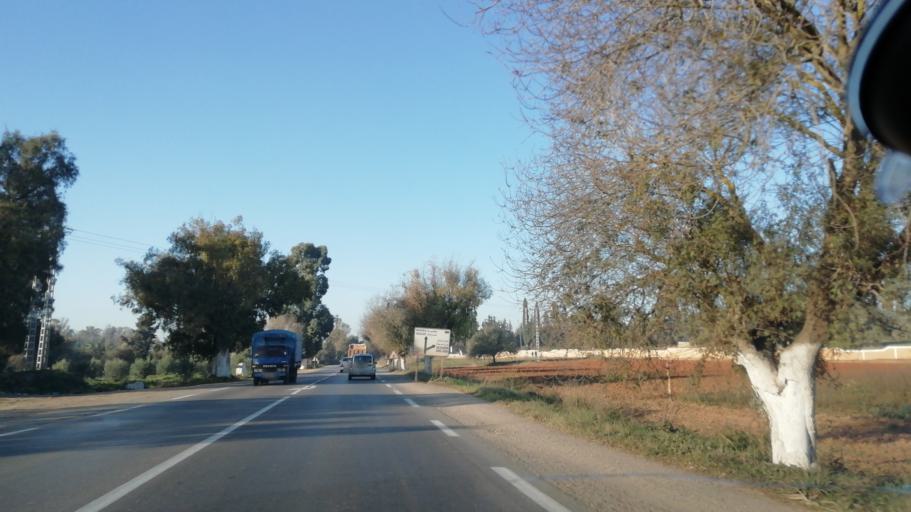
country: DZ
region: Tlemcen
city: Remchi
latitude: 35.0718
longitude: -1.4595
